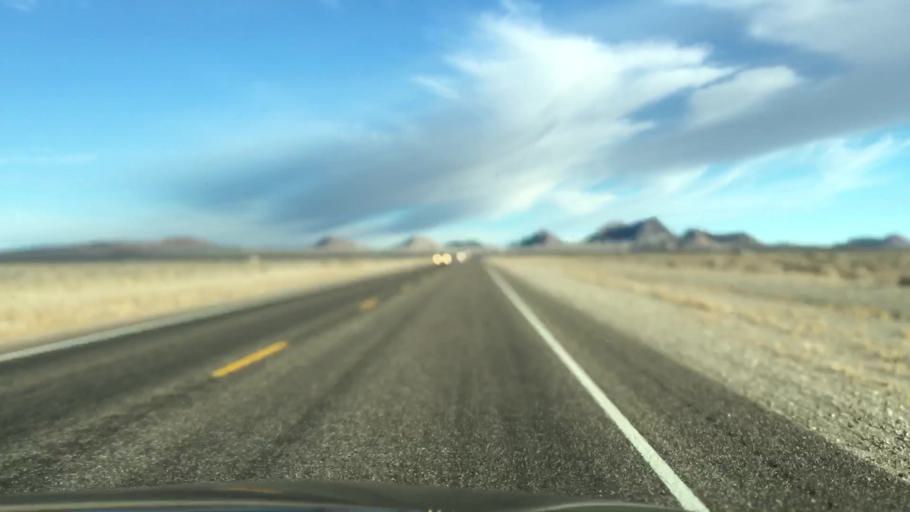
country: US
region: Nevada
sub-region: Nye County
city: Tonopah
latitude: 38.1016
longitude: -117.3335
